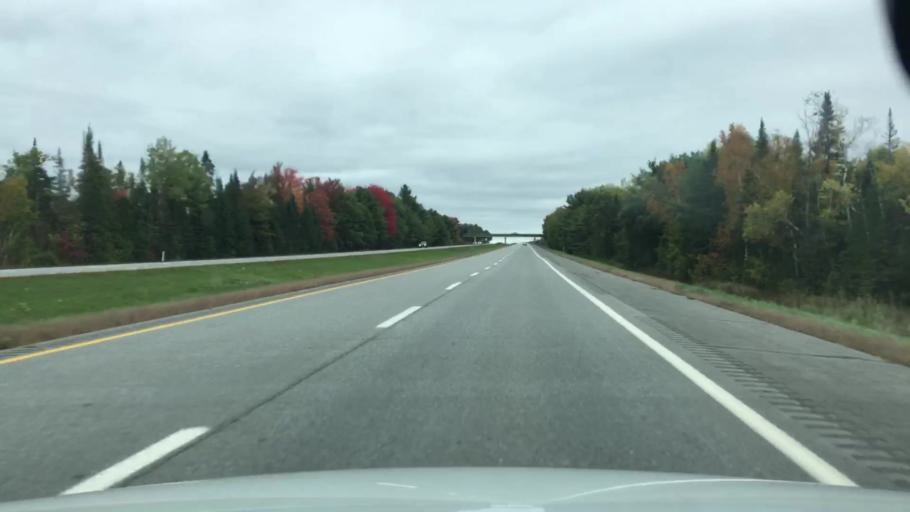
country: US
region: Maine
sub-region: Penobscot County
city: Newport
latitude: 44.8218
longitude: -69.2665
